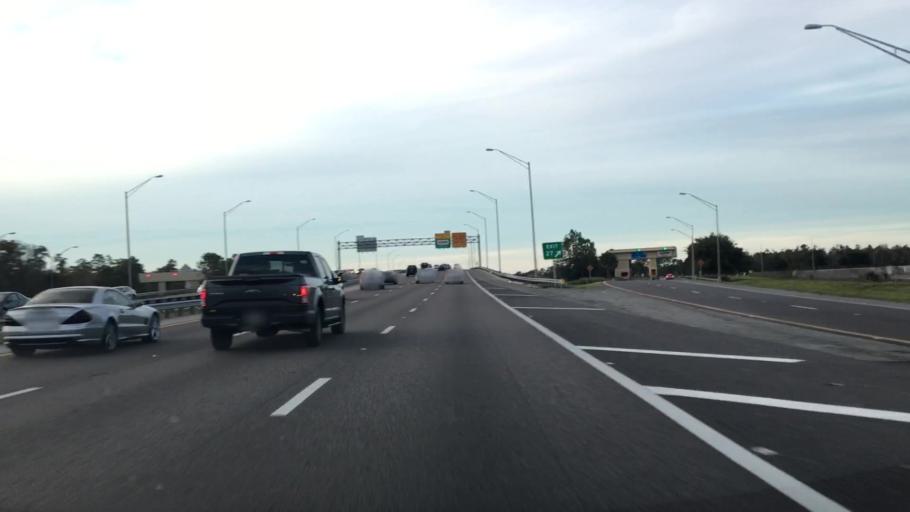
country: US
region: Florida
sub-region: Orange County
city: Azalea Park
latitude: 28.4740
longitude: -81.2384
